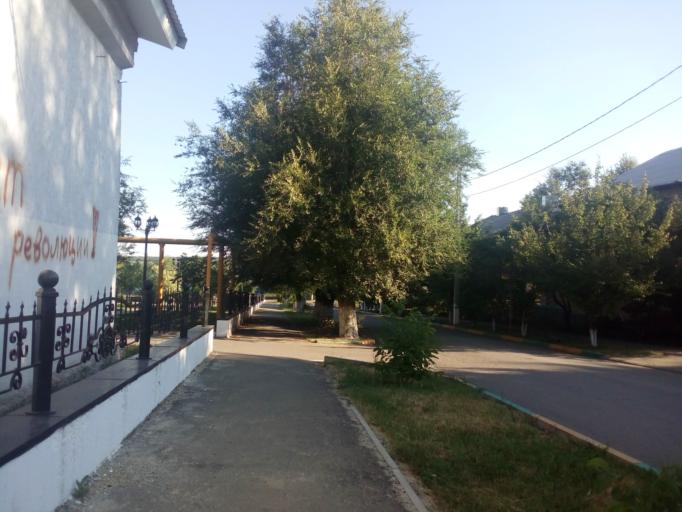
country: RU
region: Rostov
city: Sholokhovskiy
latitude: 48.2803
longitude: 41.0454
